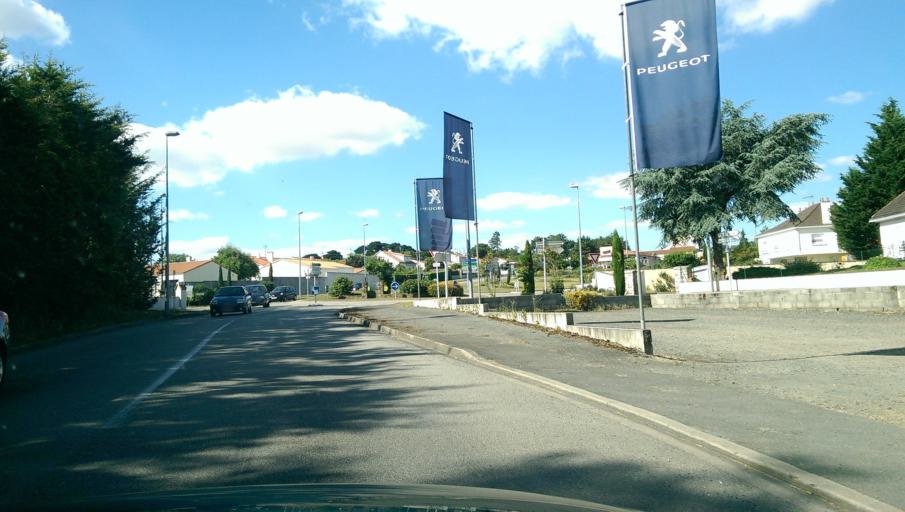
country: FR
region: Pays de la Loire
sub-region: Departement de la Vendee
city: Rocheserviere
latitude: 46.9383
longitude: -1.5140
